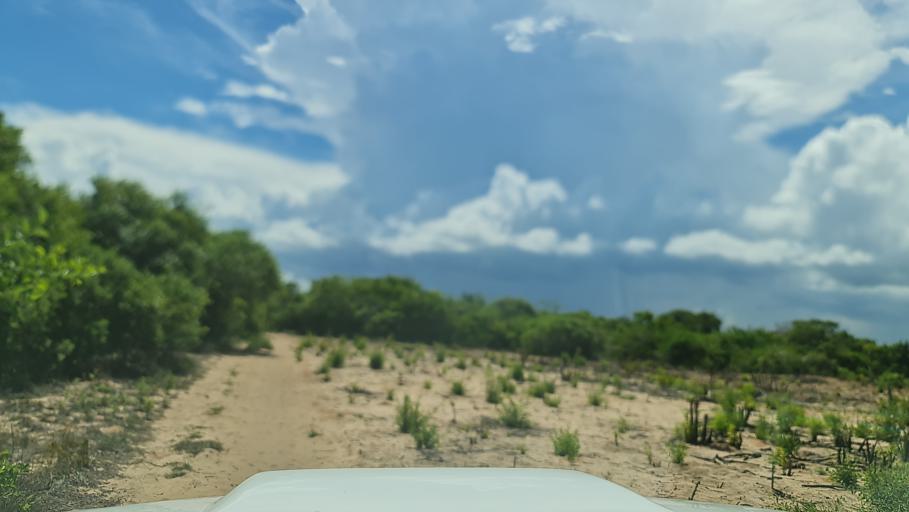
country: MZ
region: Nampula
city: Antonio Enes
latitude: -15.7072
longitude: 40.2558
